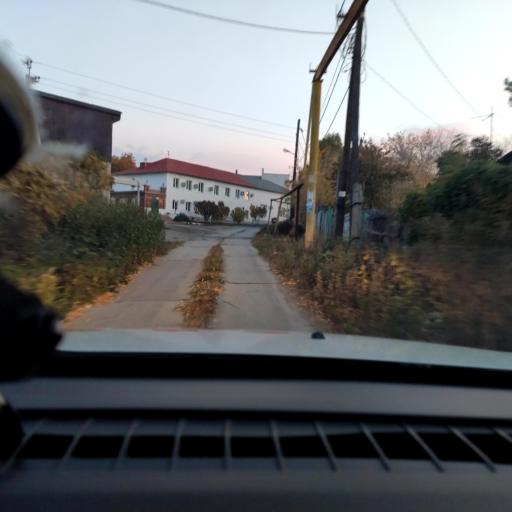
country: RU
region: Samara
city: Samara
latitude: 53.1775
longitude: 50.1607
